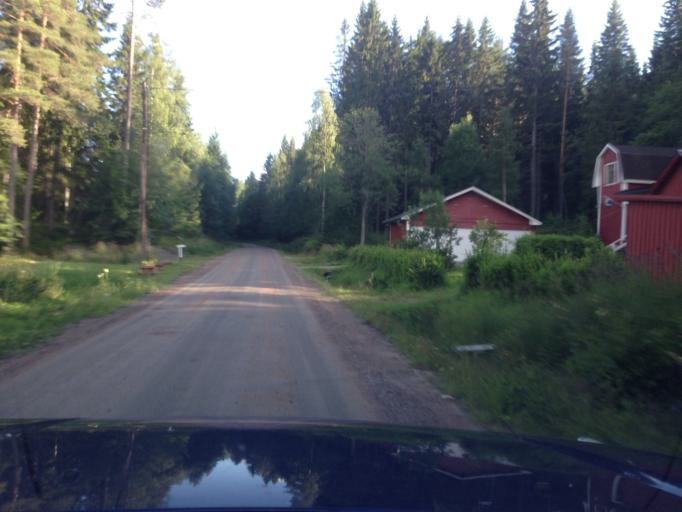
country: SE
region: Dalarna
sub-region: Ludvika Kommun
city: Abborrberget
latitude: 60.2797
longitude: 14.7240
